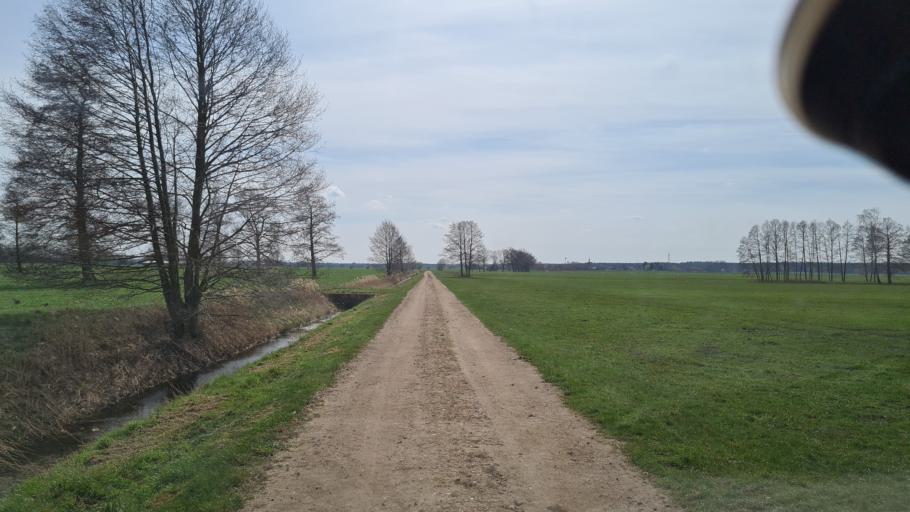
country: DE
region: Brandenburg
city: Bronkow
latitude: 51.6079
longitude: 13.9270
